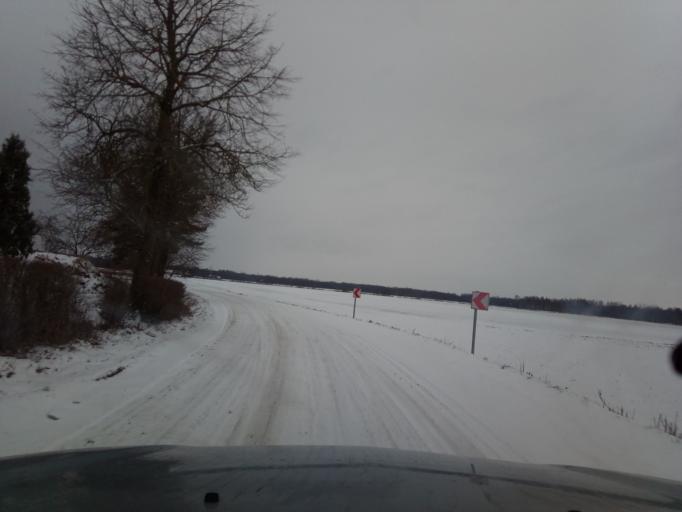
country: LT
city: Ramygala
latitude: 55.4863
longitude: 24.5825
